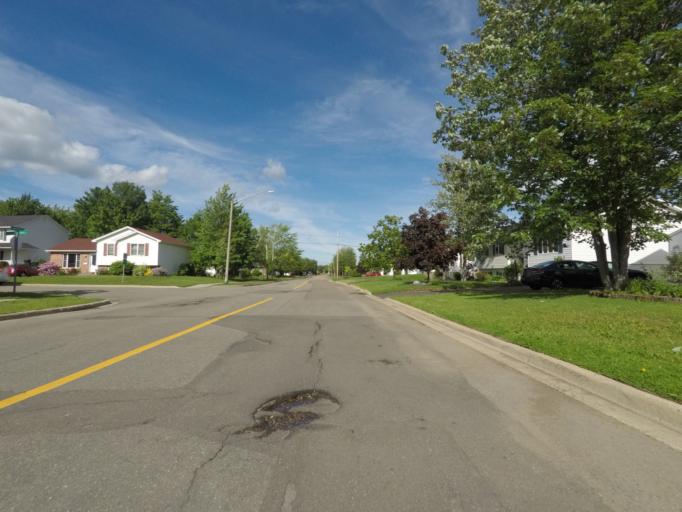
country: CA
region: New Brunswick
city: Moncton
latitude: 46.0983
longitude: -64.8312
